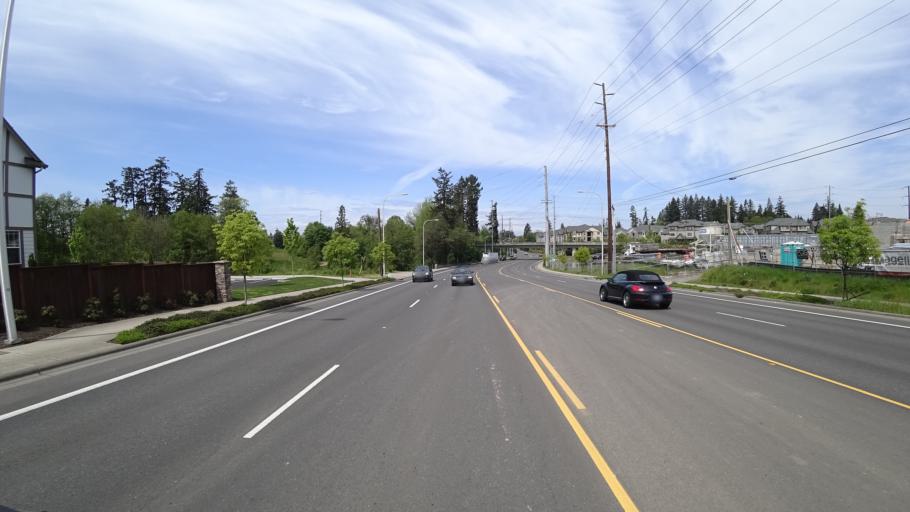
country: US
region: Oregon
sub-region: Washington County
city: Rockcreek
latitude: 45.5252
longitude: -122.9001
